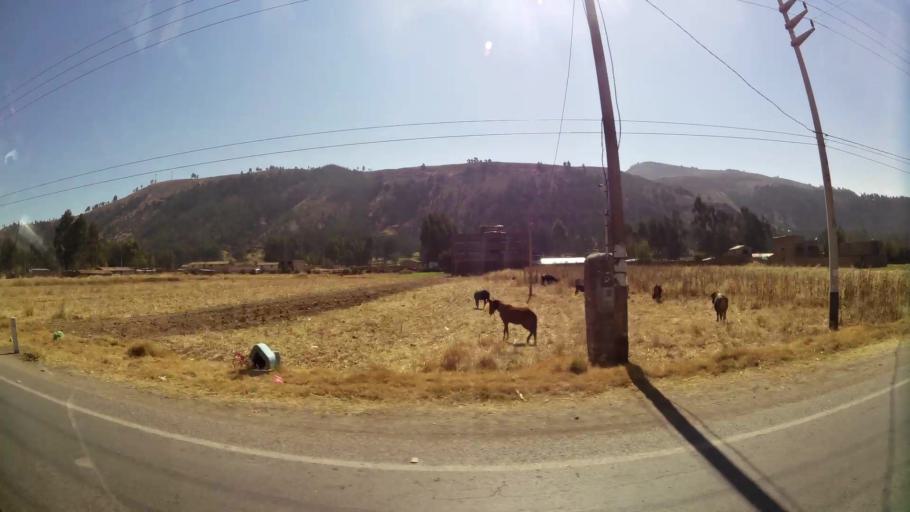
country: PE
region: Junin
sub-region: Provincia de Huancayo
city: San Jeronimo
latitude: -11.9421
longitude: -75.2985
